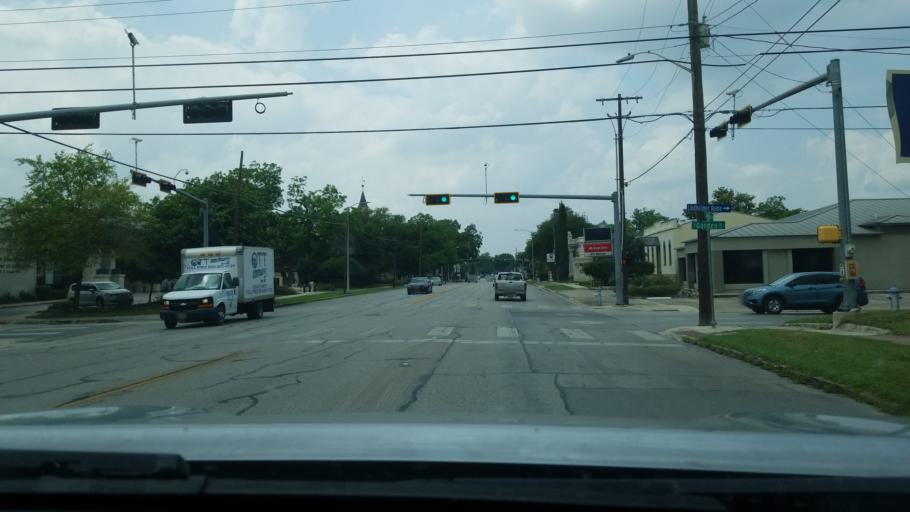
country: US
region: Texas
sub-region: Comal County
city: New Braunfels
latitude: 29.7001
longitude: -98.1205
